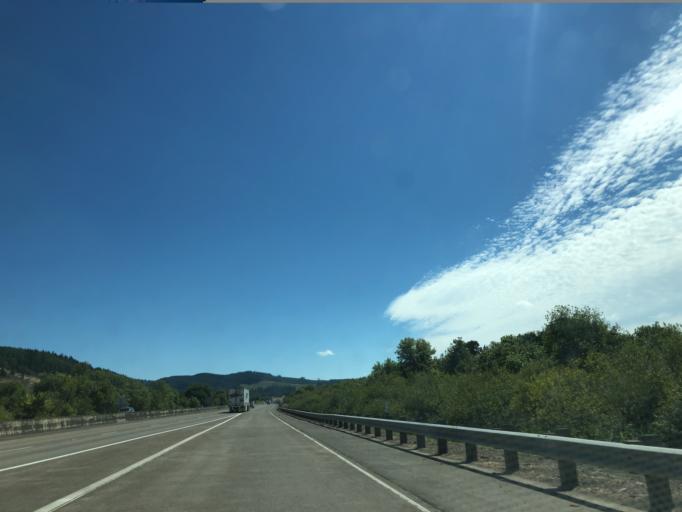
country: US
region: Oregon
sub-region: Douglas County
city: Yoncalla
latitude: 43.5615
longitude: -123.2816
